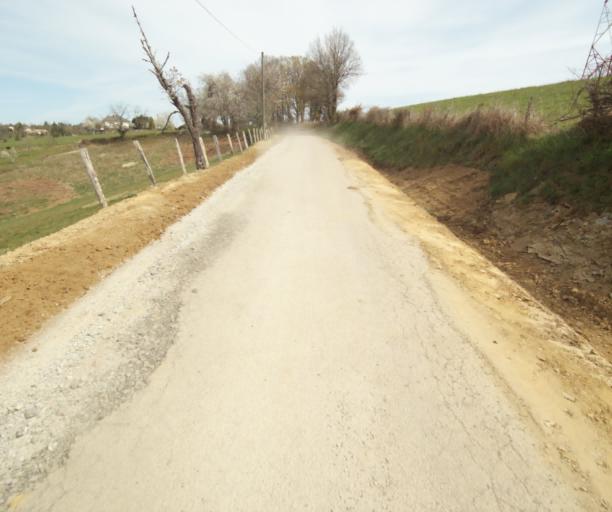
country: FR
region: Limousin
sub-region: Departement de la Correze
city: Naves
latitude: 45.2948
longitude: 1.7789
